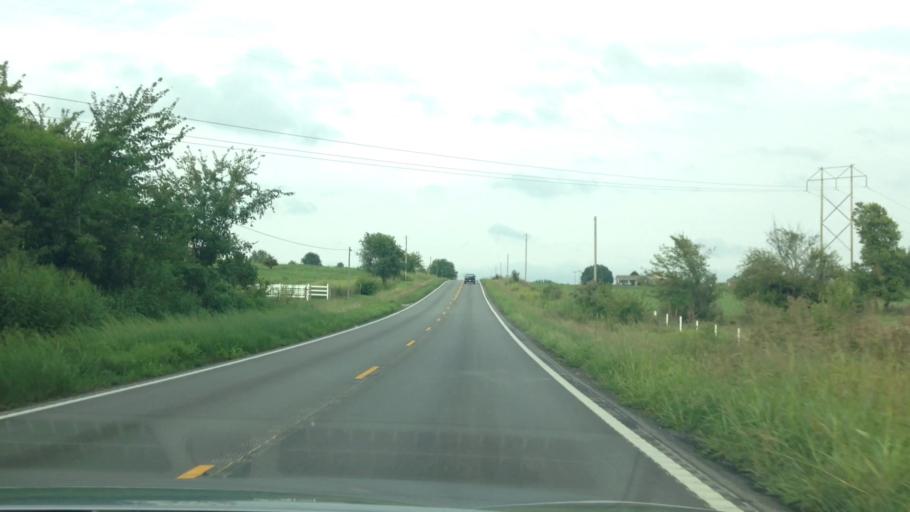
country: US
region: Missouri
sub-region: Clay County
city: Smithville
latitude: 39.3613
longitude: -94.6769
